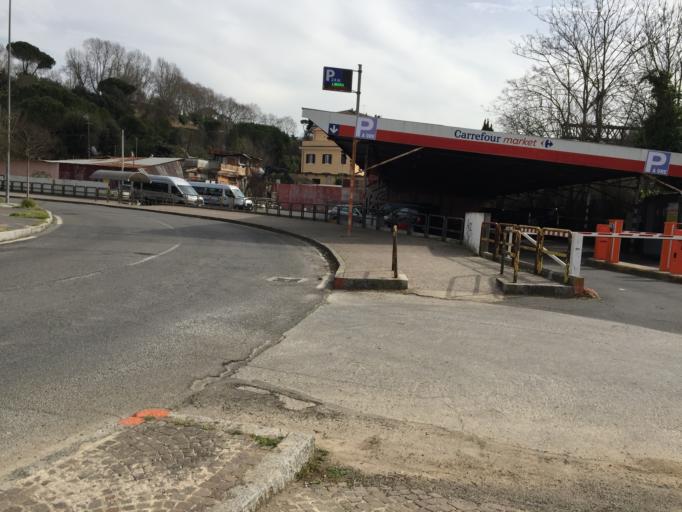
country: VA
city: Vatican City
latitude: 41.8947
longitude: 12.4565
